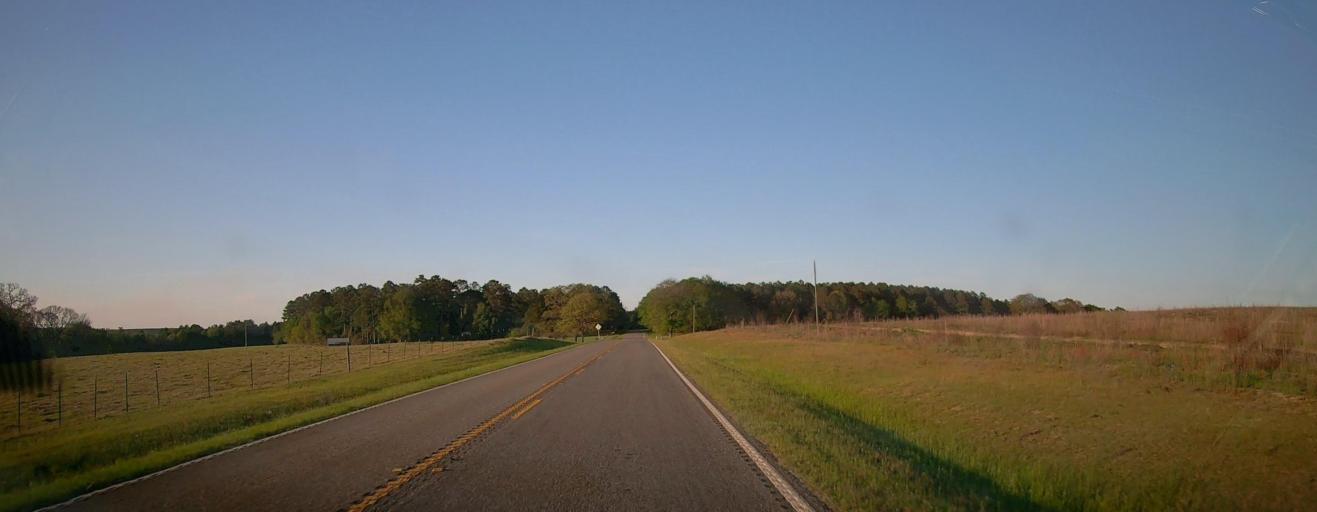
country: US
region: Georgia
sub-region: Marion County
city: Buena Vista
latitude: 32.4006
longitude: -84.4420
